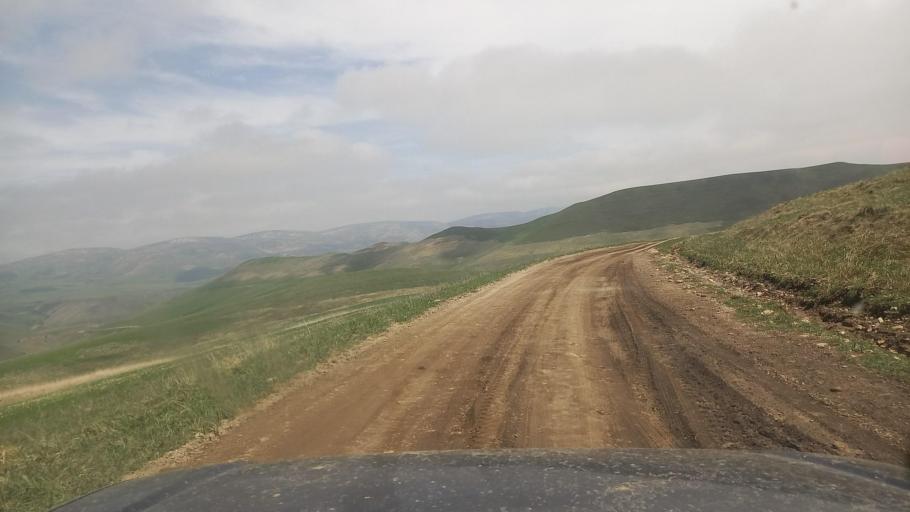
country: RU
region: Stavropol'skiy
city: Kislovodsk
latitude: 43.7799
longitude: 42.8568
